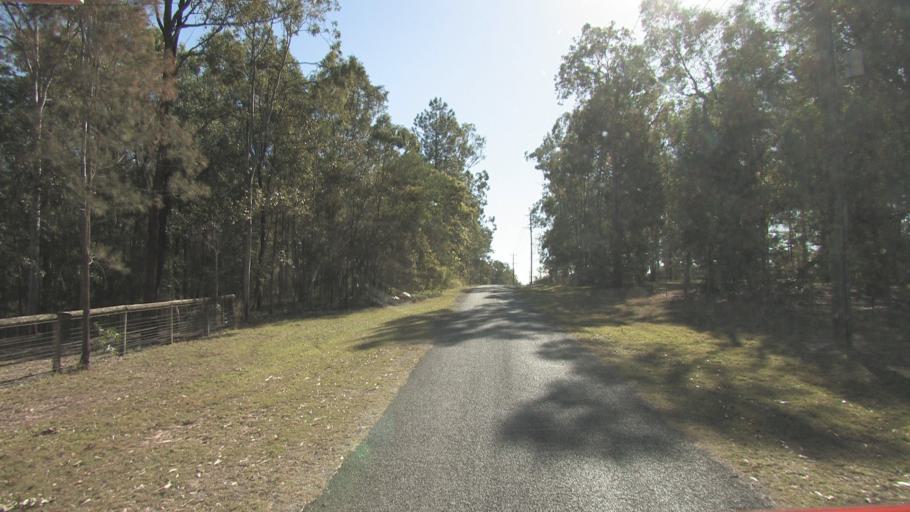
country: AU
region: Queensland
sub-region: Logan
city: Park Ridge South
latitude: -27.7527
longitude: 153.0472
